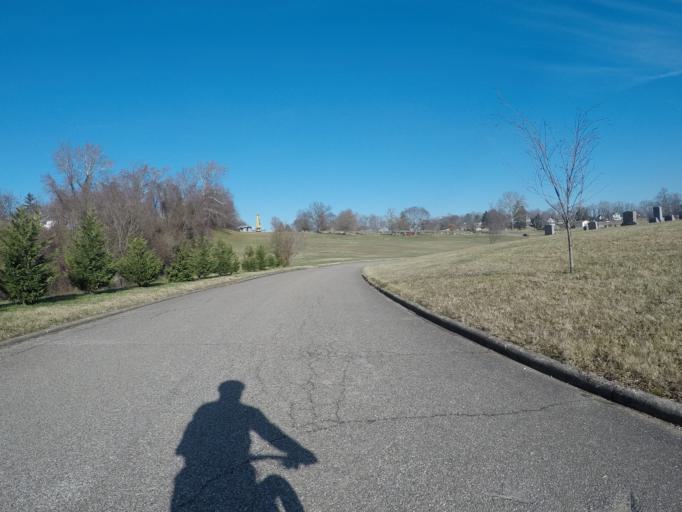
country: US
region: West Virginia
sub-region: Cabell County
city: Huntington
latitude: 38.4088
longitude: -82.4182
